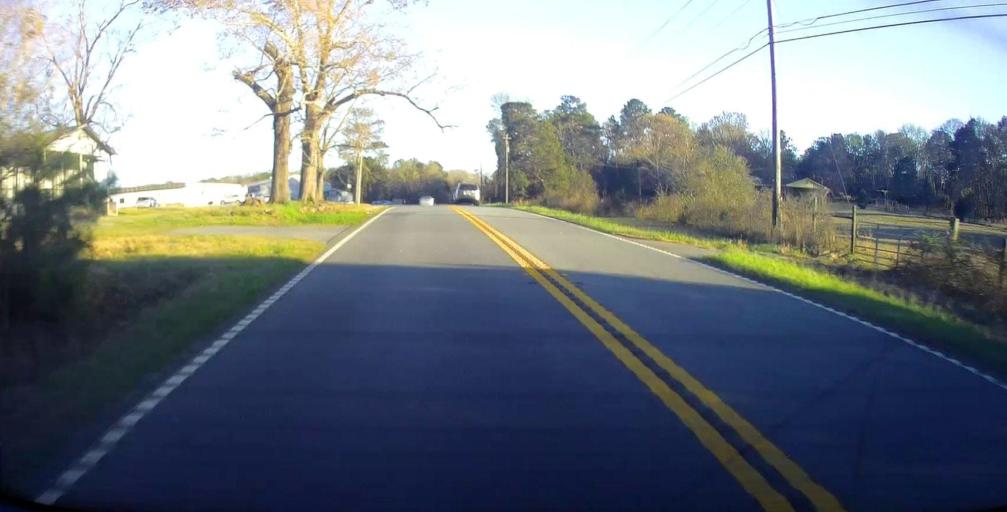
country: US
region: Georgia
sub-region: Harris County
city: Hamilton
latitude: 32.6287
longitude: -84.8230
